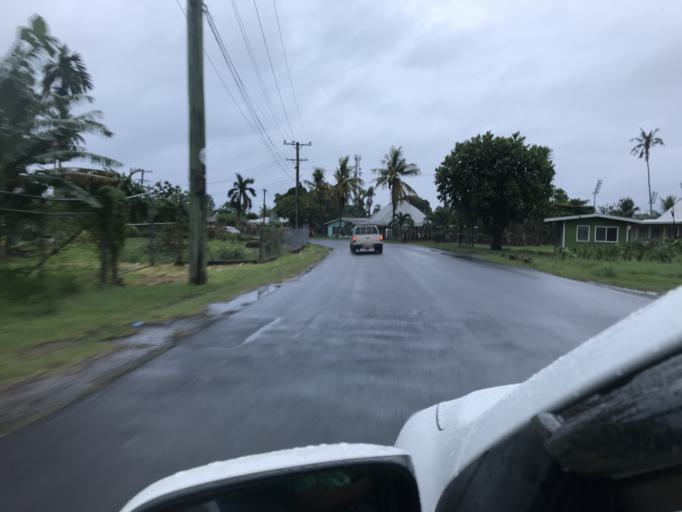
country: WS
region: Tuamasaga
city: Apia
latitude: -13.8365
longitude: -171.7559
